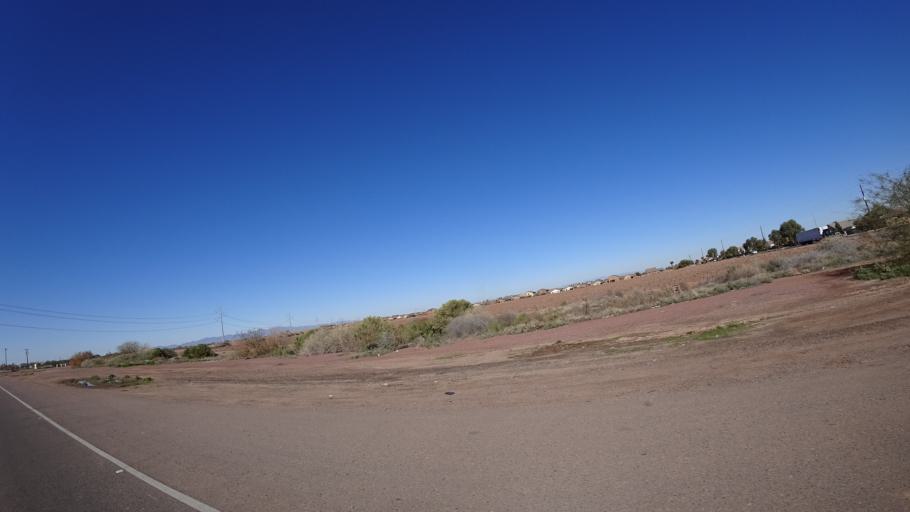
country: US
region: Arizona
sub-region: Maricopa County
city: Laveen
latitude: 33.3774
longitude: -112.2203
